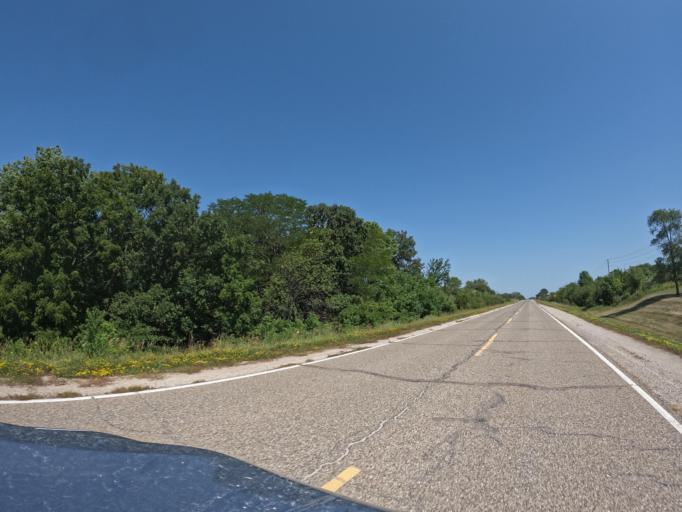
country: US
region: Iowa
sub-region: Henry County
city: Mount Pleasant
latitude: 40.9350
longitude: -91.5402
